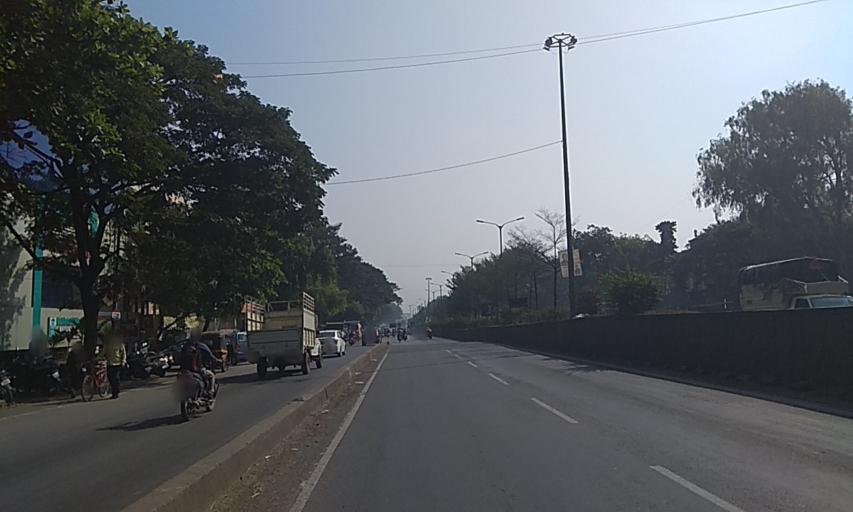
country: IN
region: Maharashtra
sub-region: Pune Division
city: Pune
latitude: 18.5006
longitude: 73.9409
